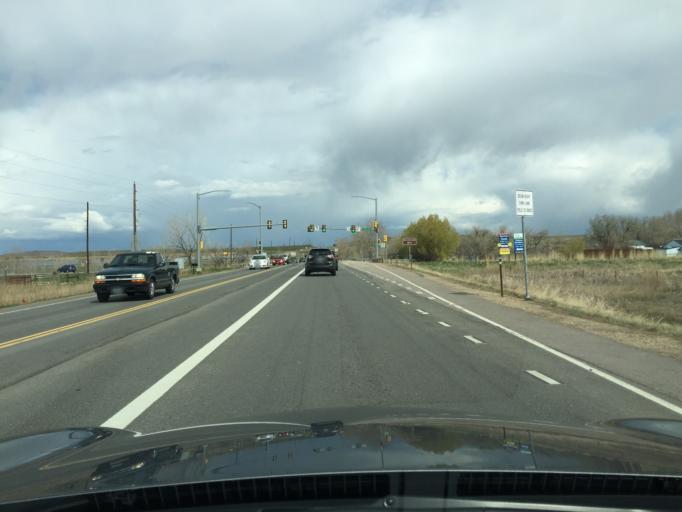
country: US
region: Colorado
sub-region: Boulder County
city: Lafayette
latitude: 40.0002
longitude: -105.0618
